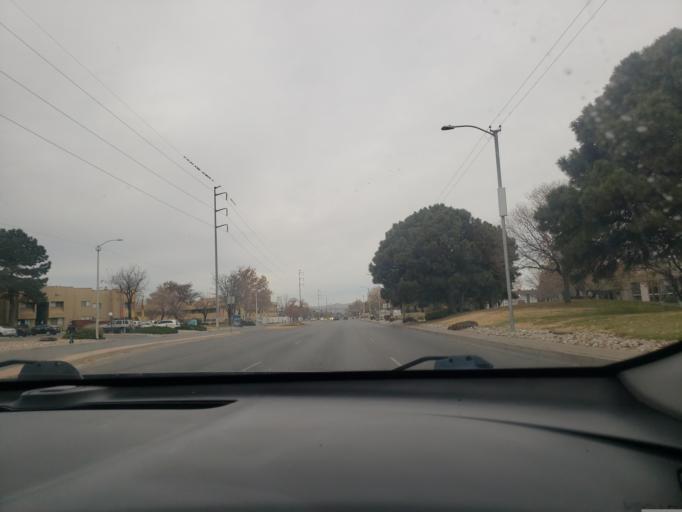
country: US
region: New Mexico
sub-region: Bernalillo County
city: North Valley
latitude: 35.1310
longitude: -106.5936
